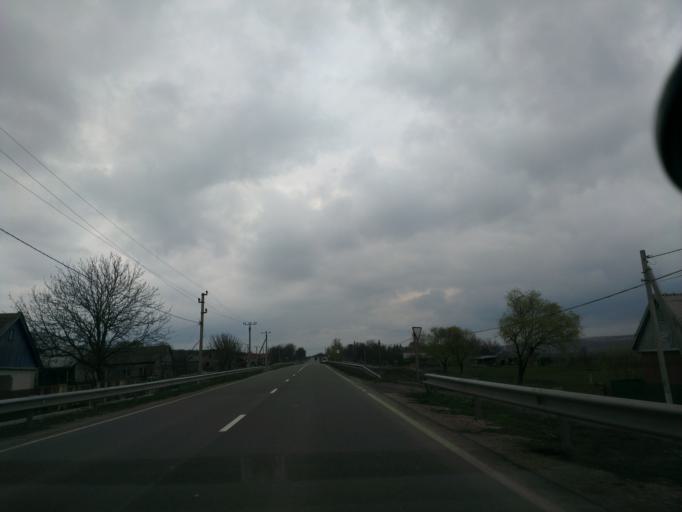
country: MD
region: Cimislia
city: Cimislia
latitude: 46.6289
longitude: 28.7208
